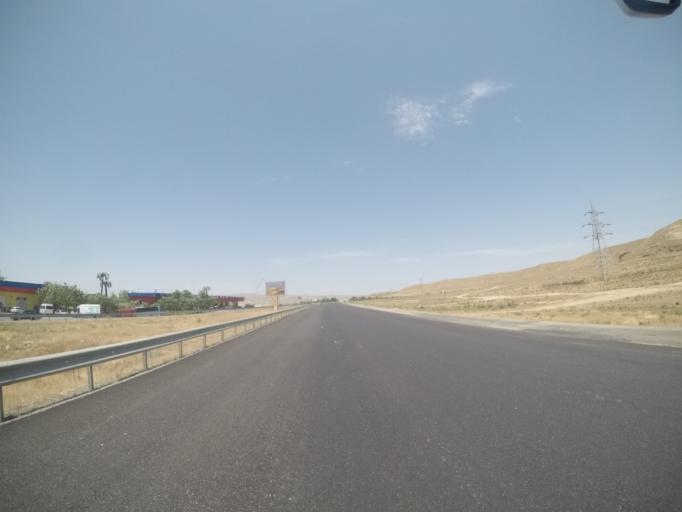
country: AZ
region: Haciqabul
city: Haciqabul
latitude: 40.0191
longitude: 48.9553
